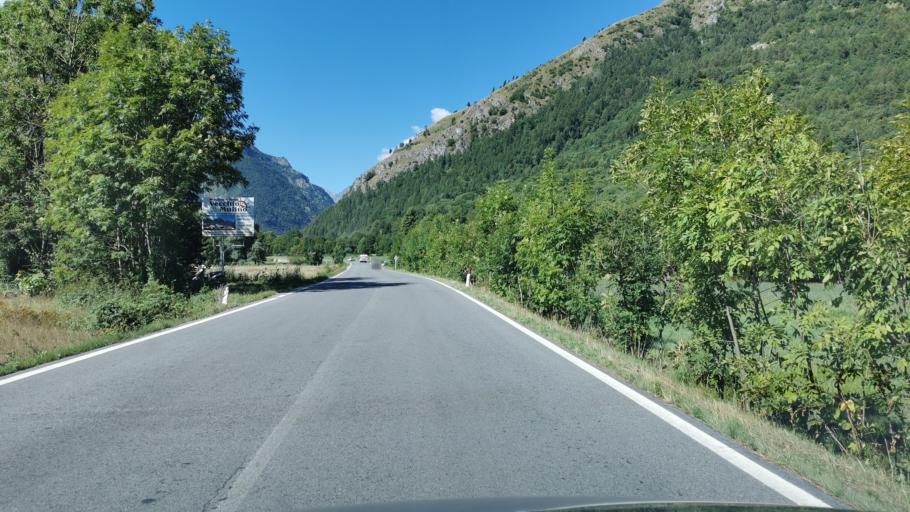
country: IT
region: Piedmont
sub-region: Provincia di Cuneo
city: Valdieri
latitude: 44.2707
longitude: 7.3921
